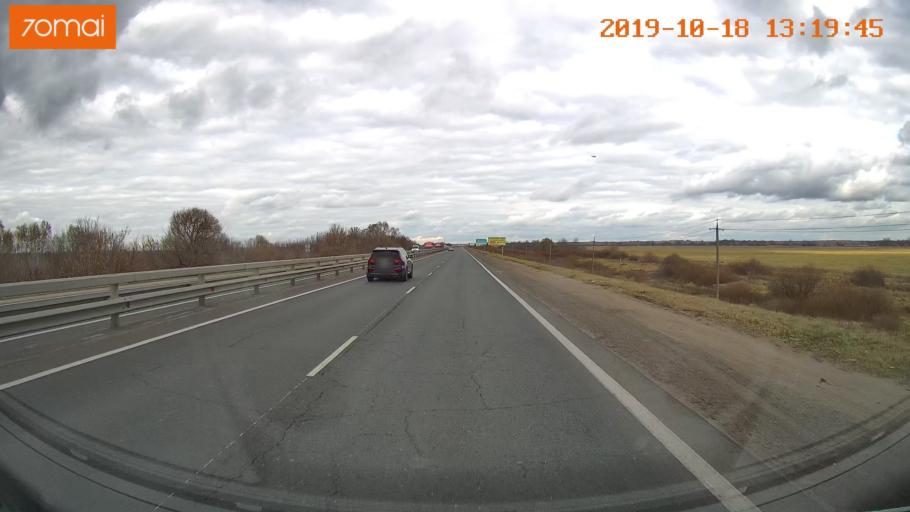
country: RU
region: Rjazan
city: Polyany
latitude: 54.6712
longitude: 39.8269
